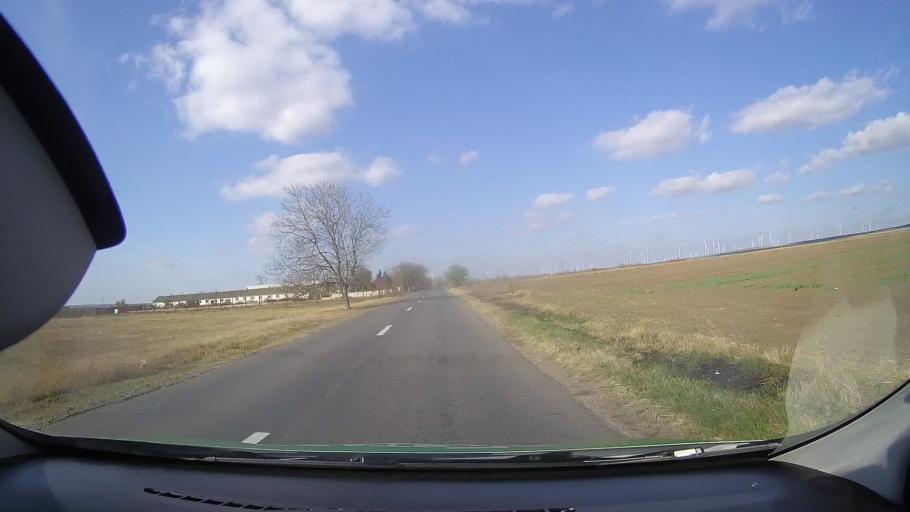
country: RO
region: Constanta
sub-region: Comuna Cogealac
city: Tariverde
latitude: 44.5605
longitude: 28.6091
